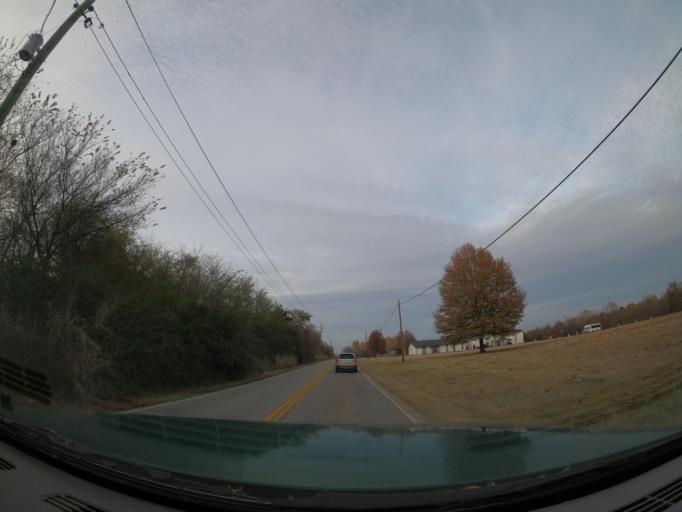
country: US
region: Oklahoma
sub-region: Tulsa County
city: Broken Arrow
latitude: 35.9836
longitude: -95.8153
